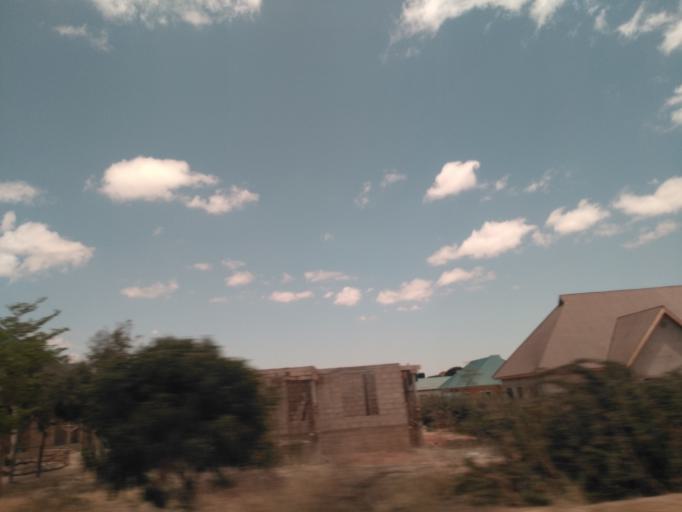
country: TZ
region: Dodoma
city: Kisasa
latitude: -6.1818
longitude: 35.7935
